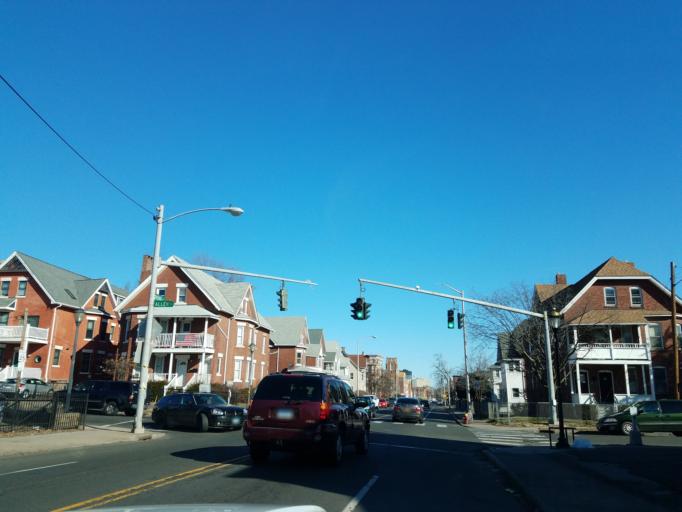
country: US
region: Connecticut
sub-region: Hartford County
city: Hartford
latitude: 41.7521
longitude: -72.6871
